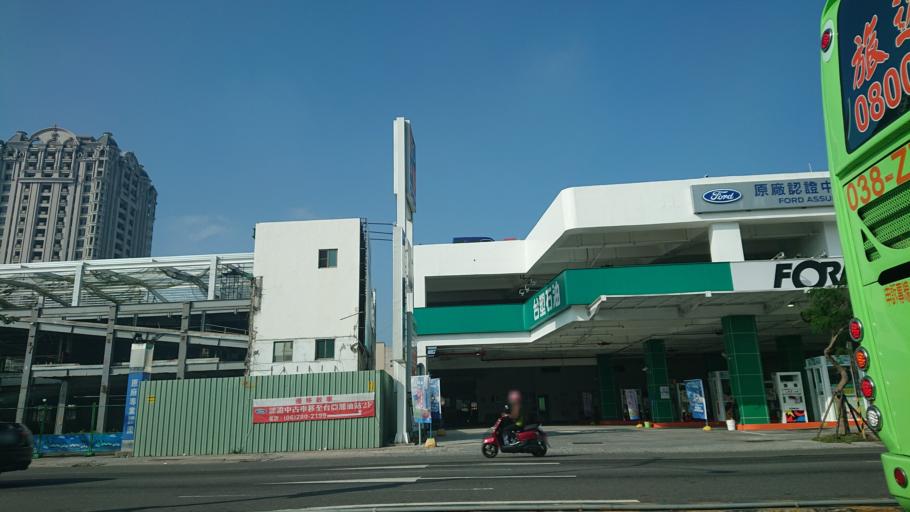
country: TW
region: Taiwan
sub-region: Tainan
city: Tainan
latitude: 23.0074
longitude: 120.1862
